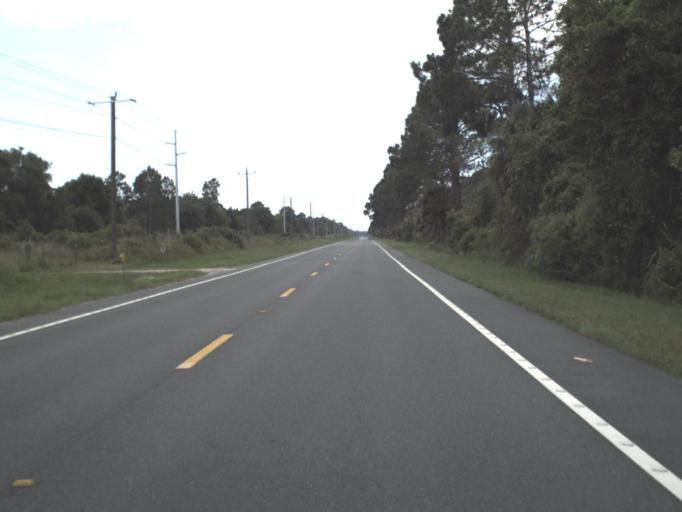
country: US
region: Florida
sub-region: Levy County
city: Chiefland
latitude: 29.1975
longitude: -82.9976
